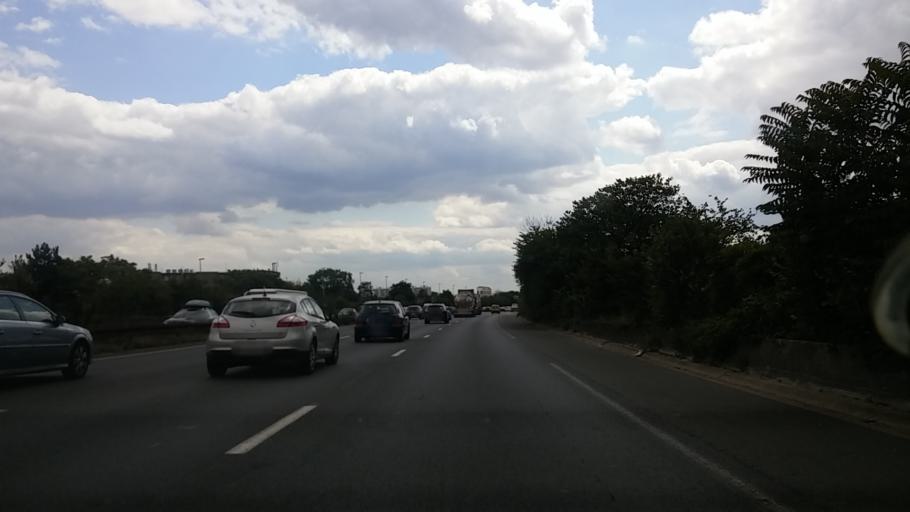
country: FR
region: Ile-de-France
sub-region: Departement de Seine-Saint-Denis
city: Aulnay-sous-Bois
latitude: 48.9280
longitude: 2.4813
